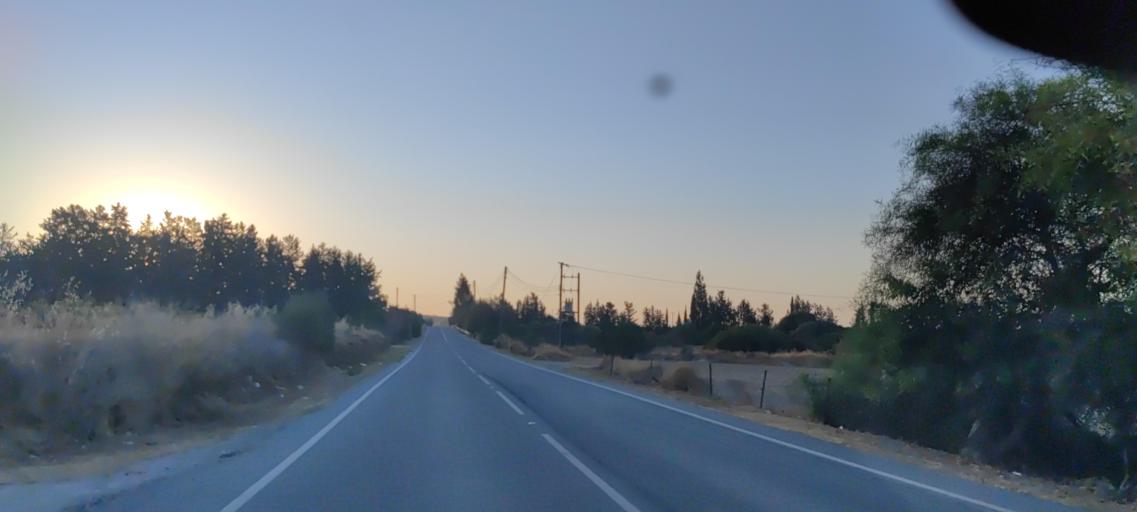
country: CY
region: Limassol
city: Pissouri
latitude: 34.6780
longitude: 32.7779
